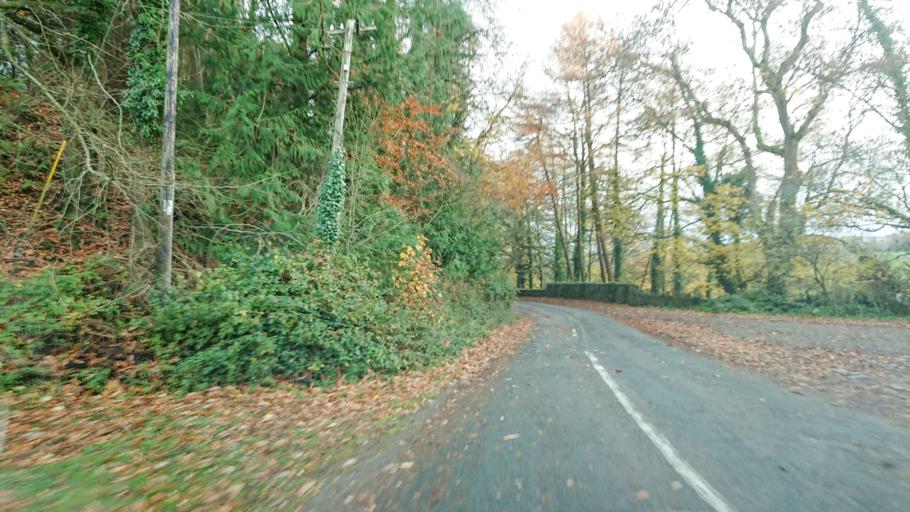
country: IE
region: Munster
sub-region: South Tipperary
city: Cluain Meala
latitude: 52.3570
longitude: -7.5973
